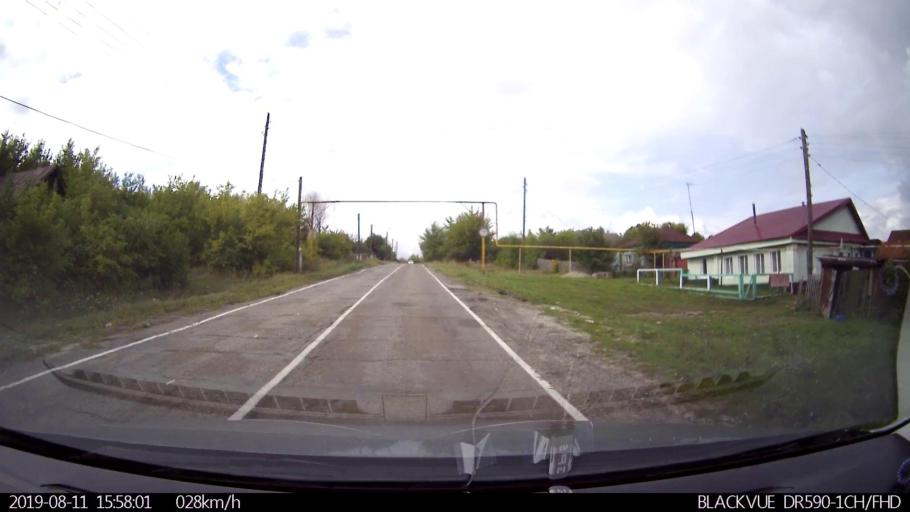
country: RU
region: Ulyanovsk
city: Ignatovka
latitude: 53.9535
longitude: 47.6505
